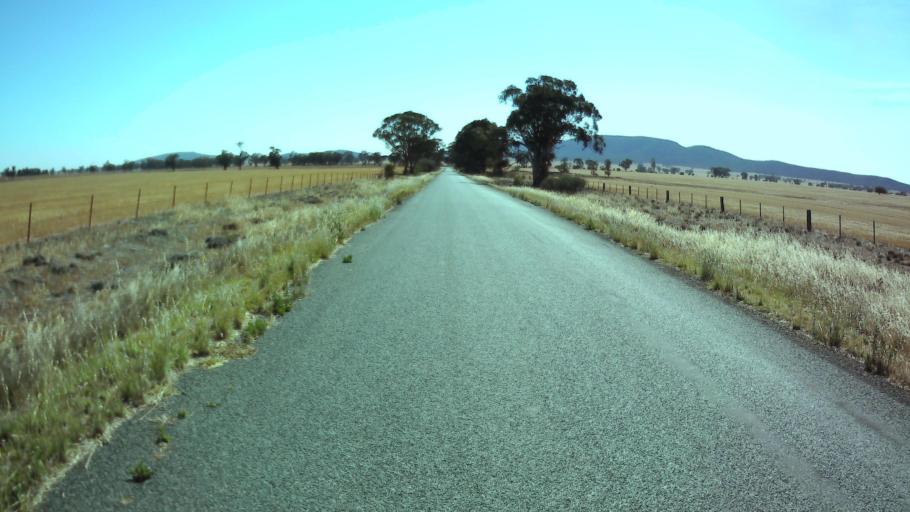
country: AU
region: New South Wales
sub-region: Weddin
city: Grenfell
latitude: -33.7511
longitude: 147.8690
